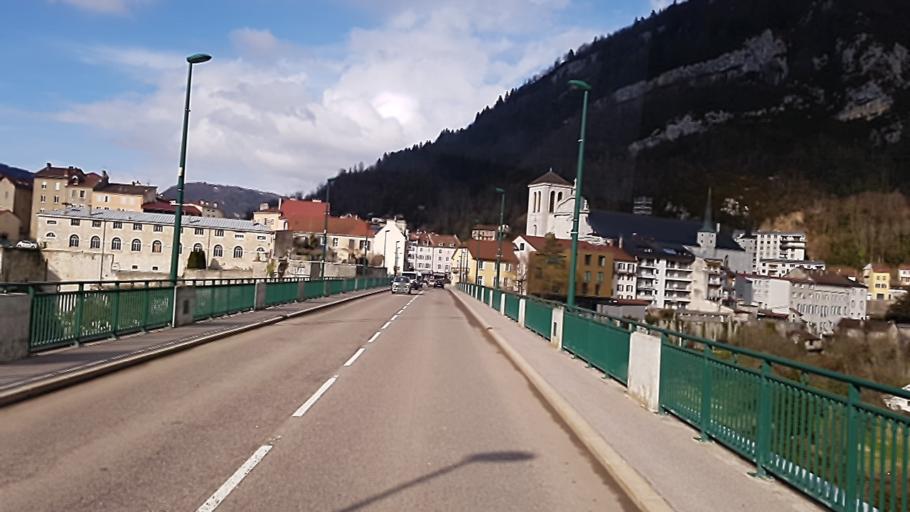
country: FR
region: Franche-Comte
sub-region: Departement du Jura
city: Saint-Claude
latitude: 46.3848
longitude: 5.8639
